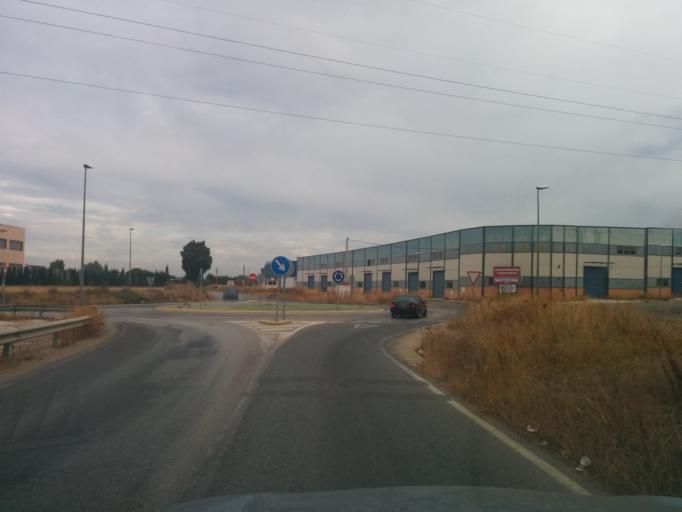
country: ES
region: Andalusia
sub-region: Provincia de Sevilla
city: La Rinconada
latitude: 37.4984
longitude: -6.0119
